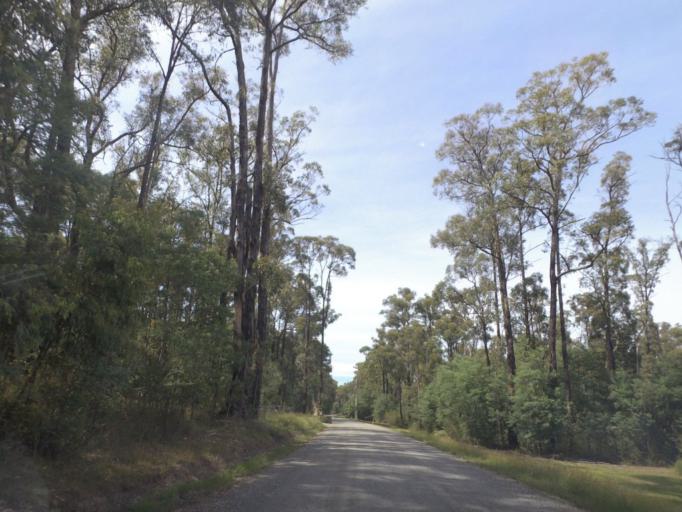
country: AU
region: Victoria
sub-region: Yarra Ranges
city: Yarra Glen
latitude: -37.5167
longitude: 145.4289
